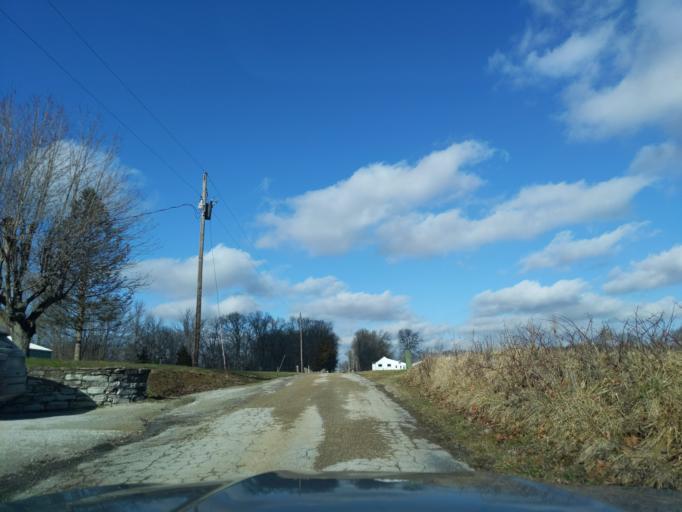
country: US
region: Indiana
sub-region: Decatur County
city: Greensburg
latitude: 39.2549
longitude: -85.4842
